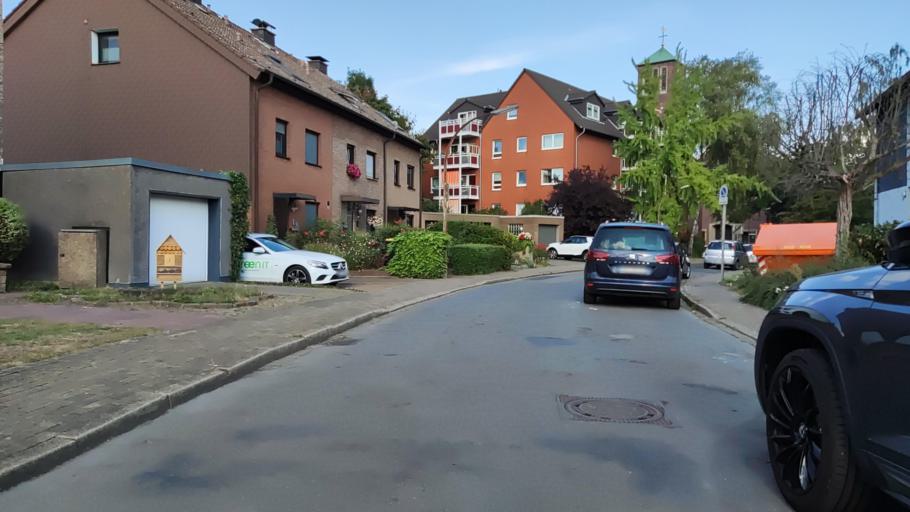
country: DE
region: North Rhine-Westphalia
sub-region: Regierungsbezirk Arnsberg
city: Herne
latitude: 51.5410
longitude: 7.2127
